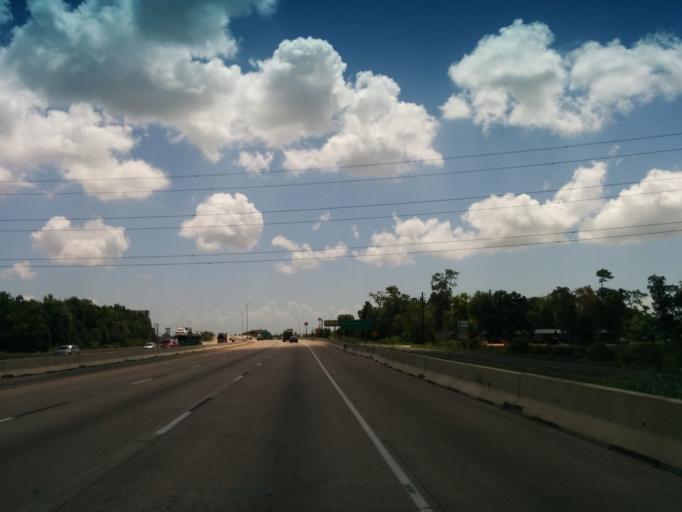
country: US
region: Texas
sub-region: Chambers County
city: Mont Belvieu
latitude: 29.8210
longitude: -94.9076
